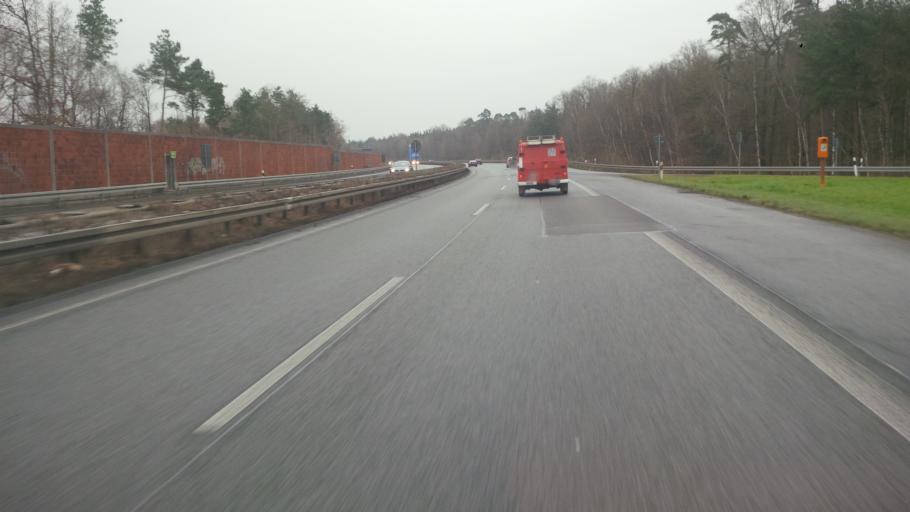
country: DE
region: Hesse
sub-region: Regierungsbezirk Giessen
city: Giessen
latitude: 50.5783
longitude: 8.7098
